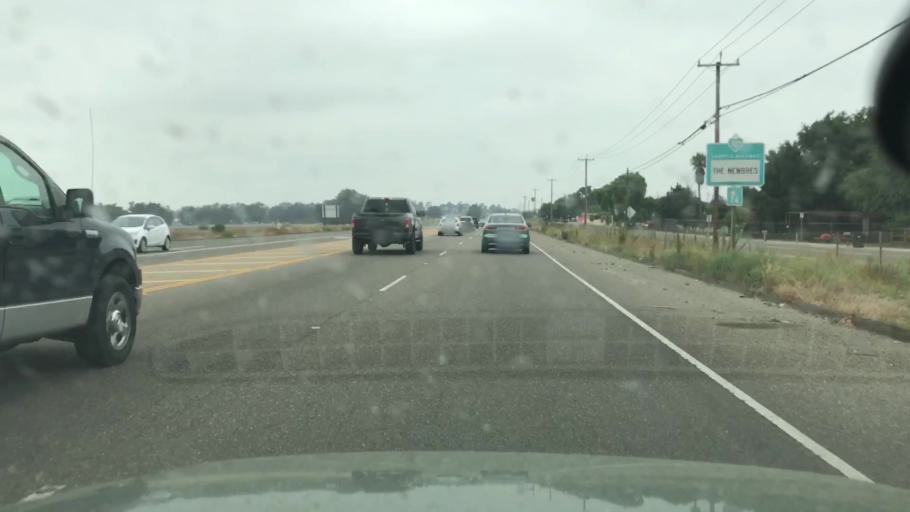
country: US
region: California
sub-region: Santa Barbara County
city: Orcutt
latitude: 34.8833
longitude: -120.4364
